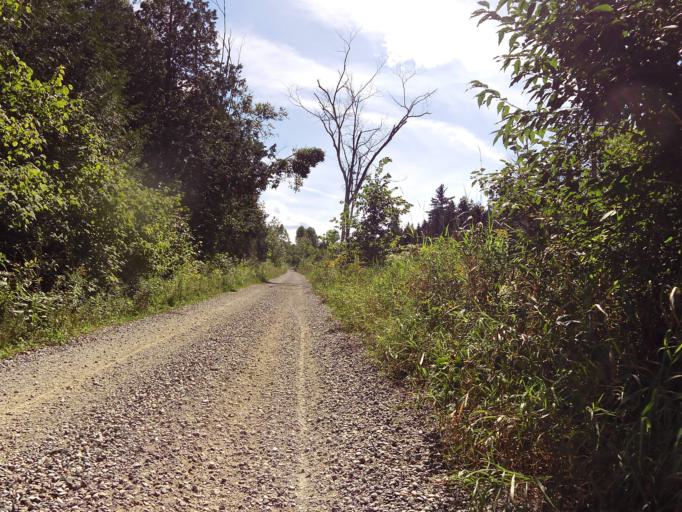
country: CA
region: Ontario
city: Renfrew
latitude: 45.0387
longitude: -76.7031
